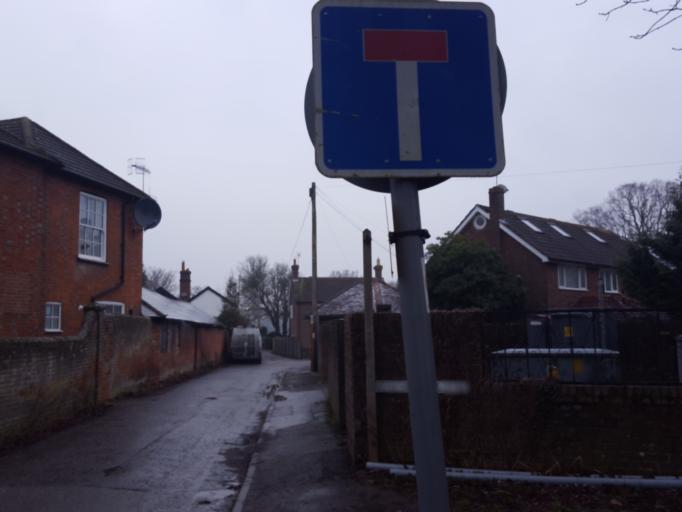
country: GB
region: England
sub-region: West Sussex
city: Langley Green
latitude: 51.1554
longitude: -0.2239
